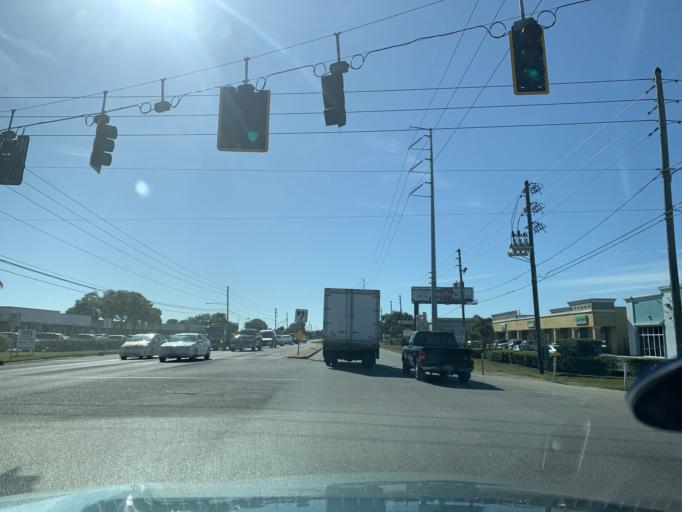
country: US
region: Florida
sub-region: Pinellas County
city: Largo
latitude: 27.8873
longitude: -82.7624
